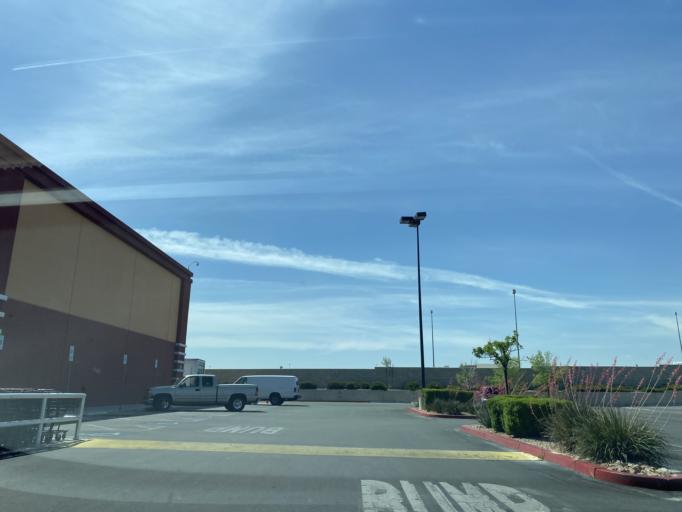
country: US
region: Nevada
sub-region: Clark County
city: Paradise
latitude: 36.0650
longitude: -115.1755
